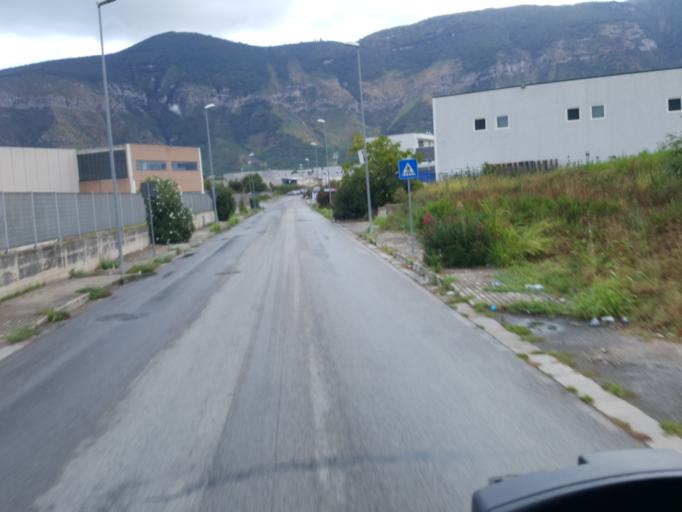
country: IT
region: Campania
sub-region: Provincia di Salerno
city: Sarno
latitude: 40.8156
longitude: 14.5999
